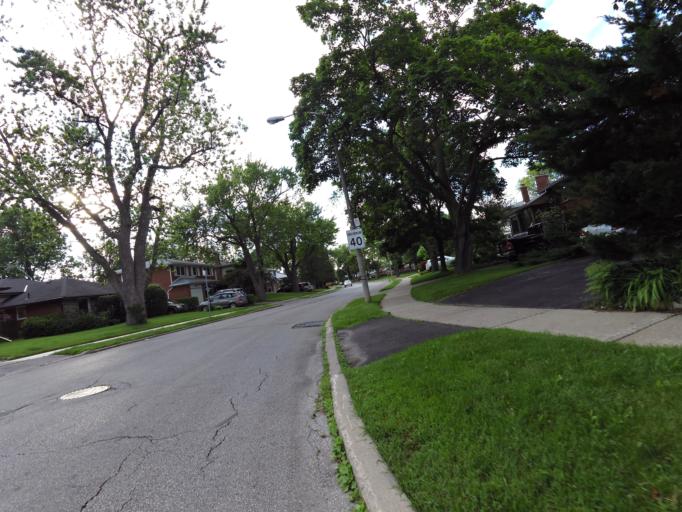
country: CA
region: Ontario
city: Scarborough
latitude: 43.7225
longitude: -79.2296
